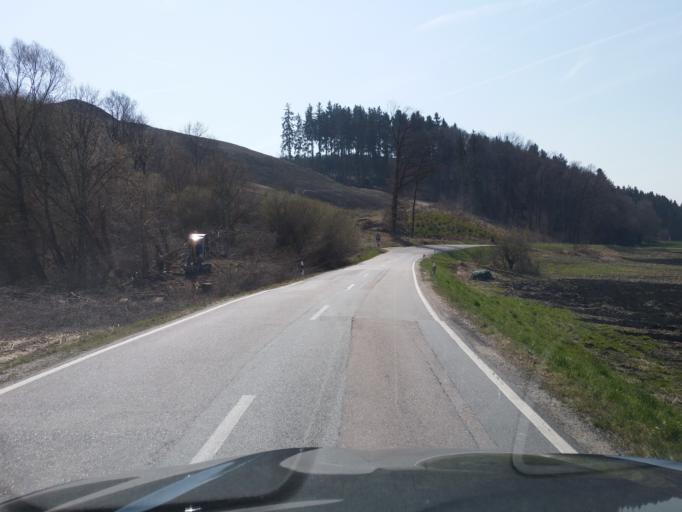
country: DE
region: Bavaria
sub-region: Upper Bavaria
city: Langenpreising
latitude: 48.4530
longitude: 12.0020
